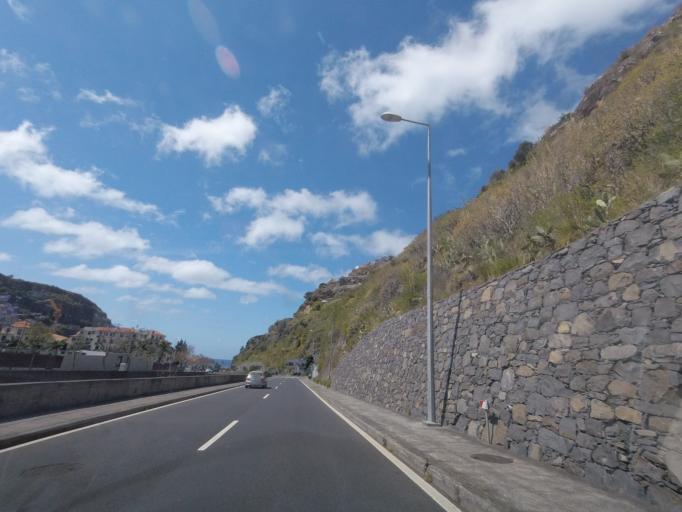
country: PT
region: Madeira
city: Ribeira Brava
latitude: 32.6763
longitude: -17.0635
